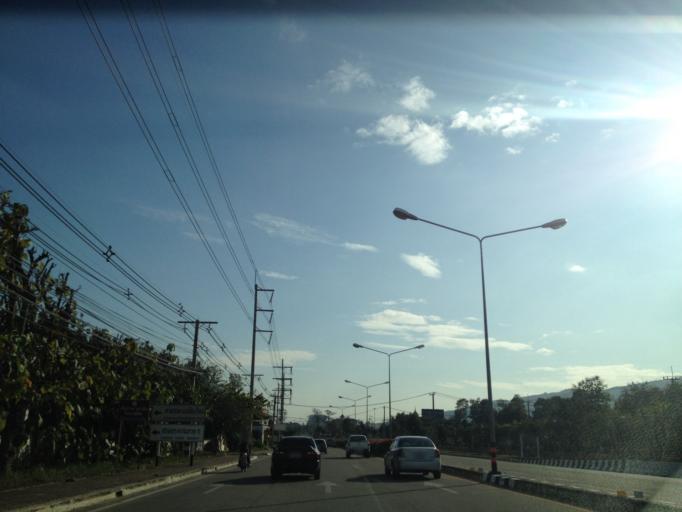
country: TH
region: Chiang Mai
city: Chiang Mai
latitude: 18.8363
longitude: 98.9643
